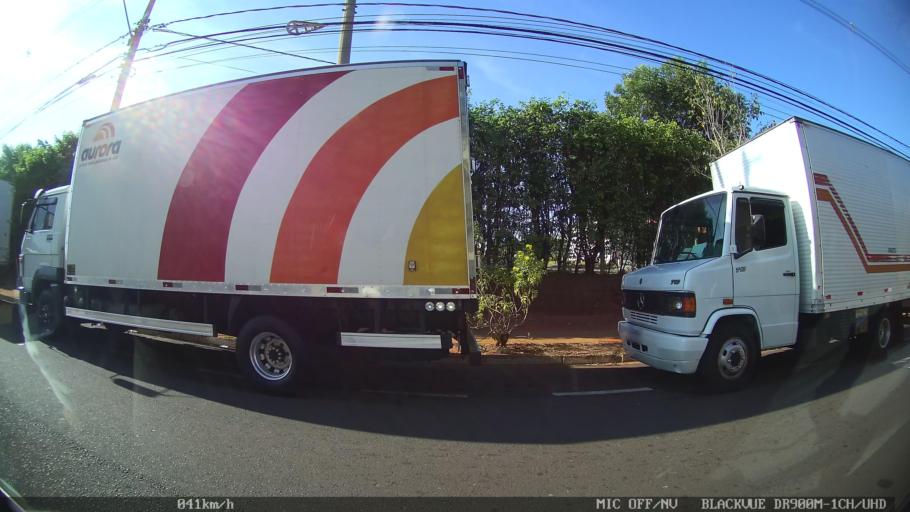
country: BR
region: Sao Paulo
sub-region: Sao Jose Do Rio Preto
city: Sao Jose do Rio Preto
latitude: -20.7721
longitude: -49.3318
